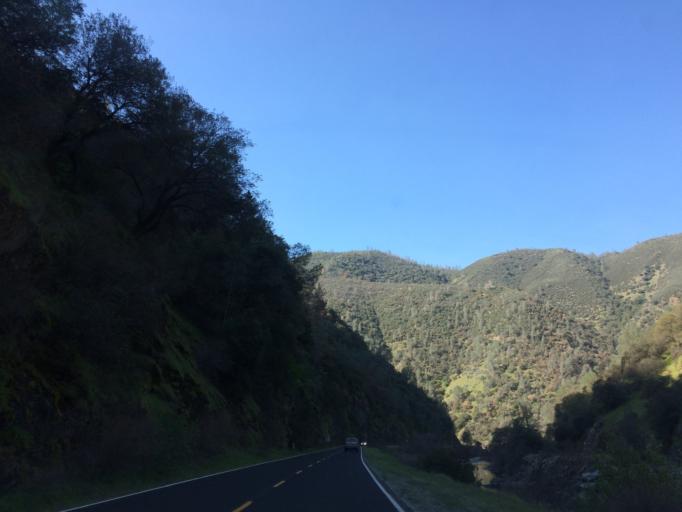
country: US
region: California
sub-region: Mariposa County
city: Midpines
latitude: 37.6689
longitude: -119.9164
